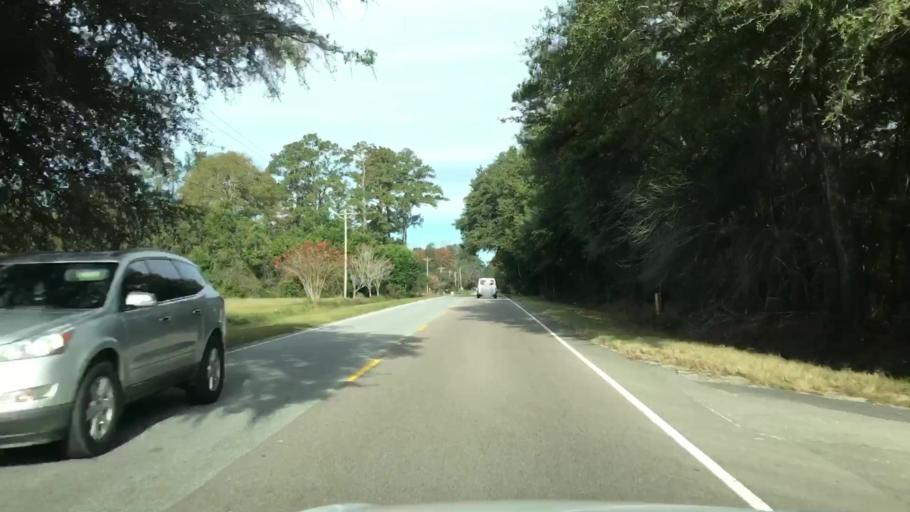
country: US
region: South Carolina
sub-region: Colleton County
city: Walterboro
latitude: 32.8495
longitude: -80.5940
